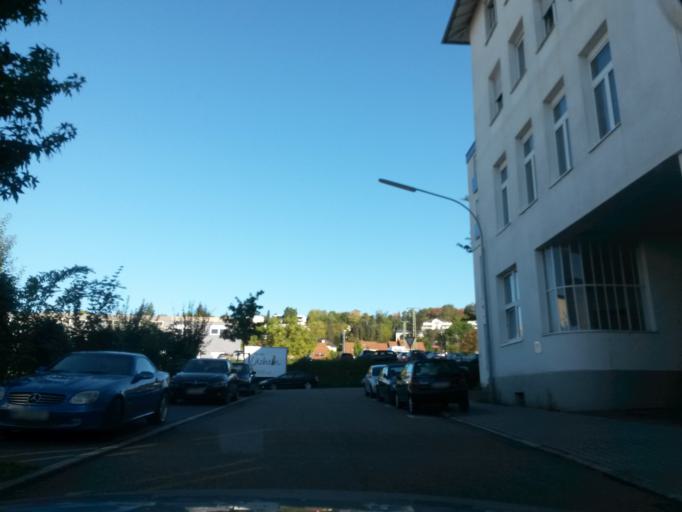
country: DE
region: Baden-Wuerttemberg
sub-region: Karlsruhe Region
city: Pforzheim
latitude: 48.8942
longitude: 8.6862
